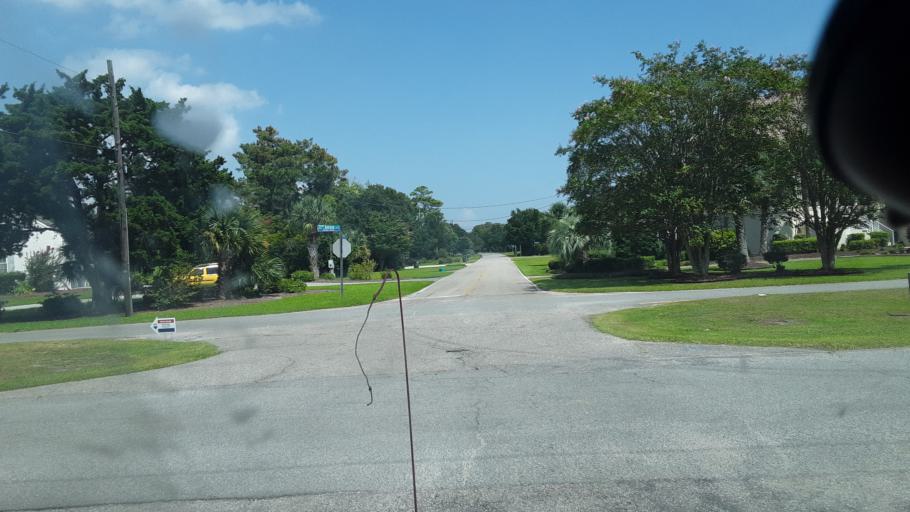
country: US
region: South Carolina
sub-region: Horry County
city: North Myrtle Beach
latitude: 33.8246
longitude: -78.6605
